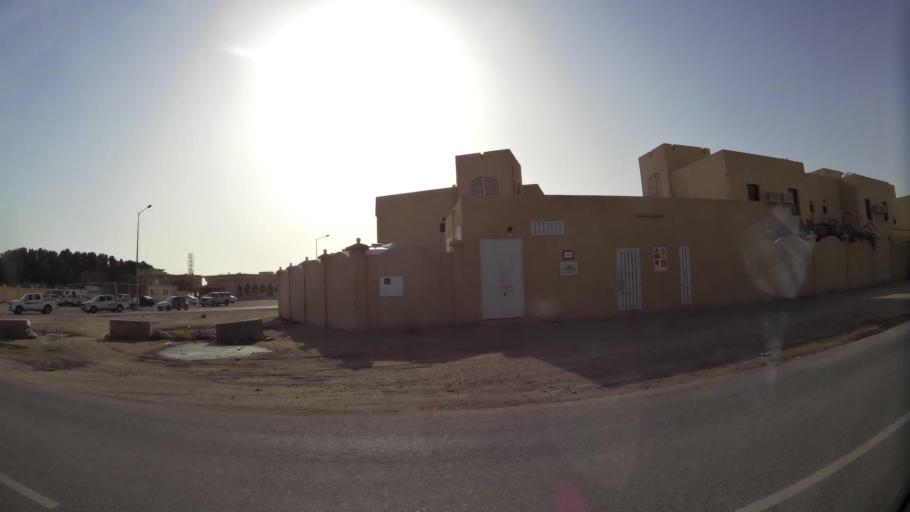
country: QA
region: Baladiyat ar Rayyan
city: Ar Rayyan
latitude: 25.3304
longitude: 51.4415
